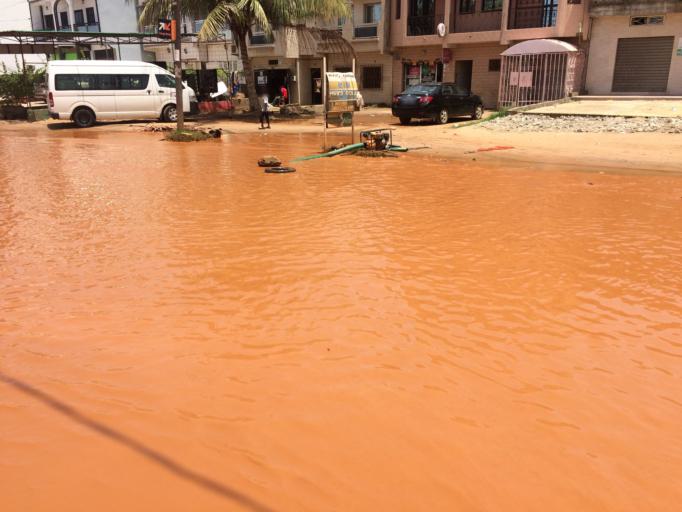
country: SN
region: Dakar
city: Pikine
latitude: 14.7369
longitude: -17.3336
